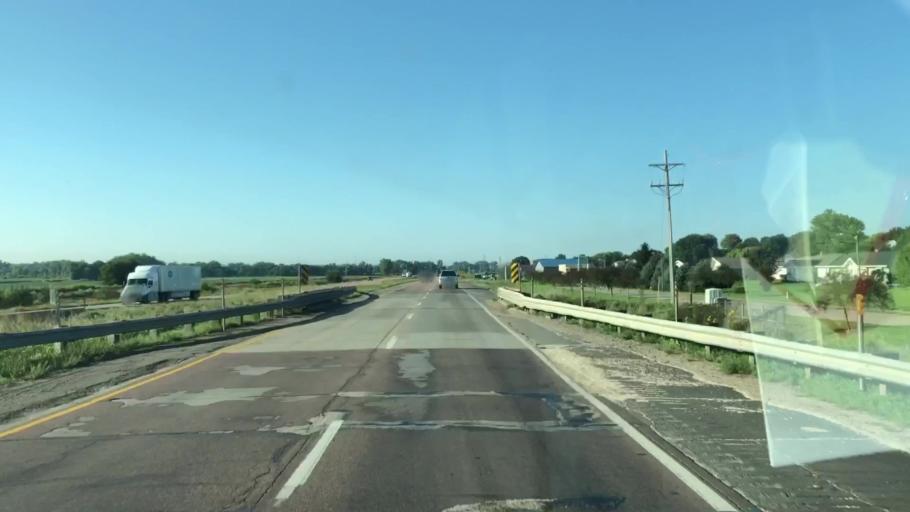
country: US
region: Iowa
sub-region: Woodbury County
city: Sioux City
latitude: 42.6188
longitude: -96.2945
